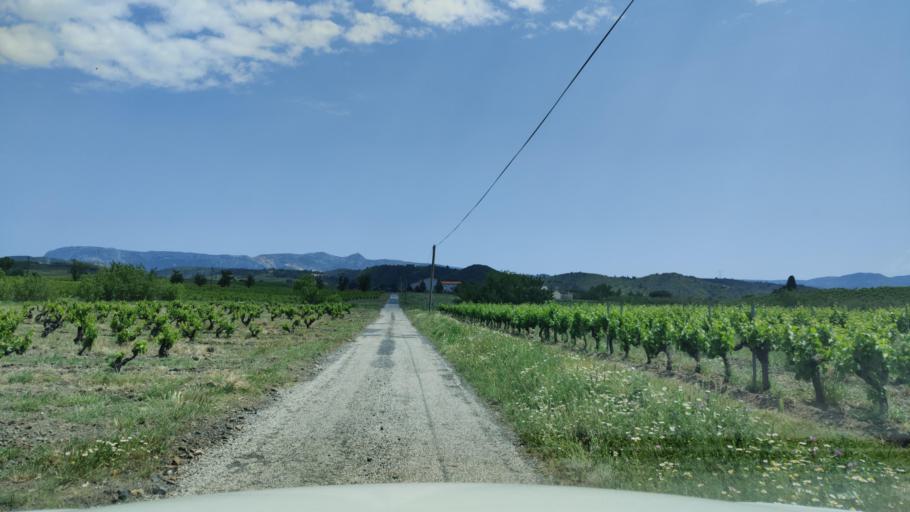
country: FR
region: Languedoc-Roussillon
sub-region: Departement des Pyrenees-Orientales
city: Estagel
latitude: 42.8157
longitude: 2.6724
